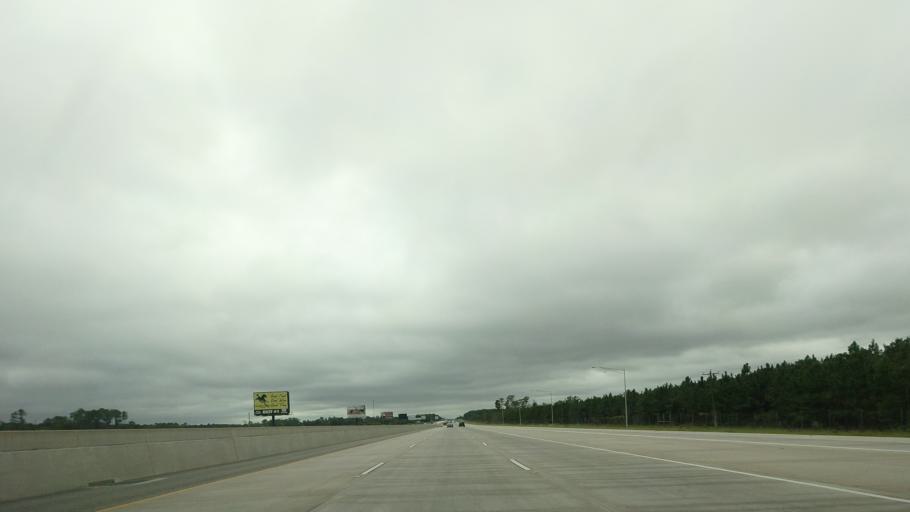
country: US
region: Georgia
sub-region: Cook County
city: Sparks
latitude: 31.2586
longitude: -83.4699
